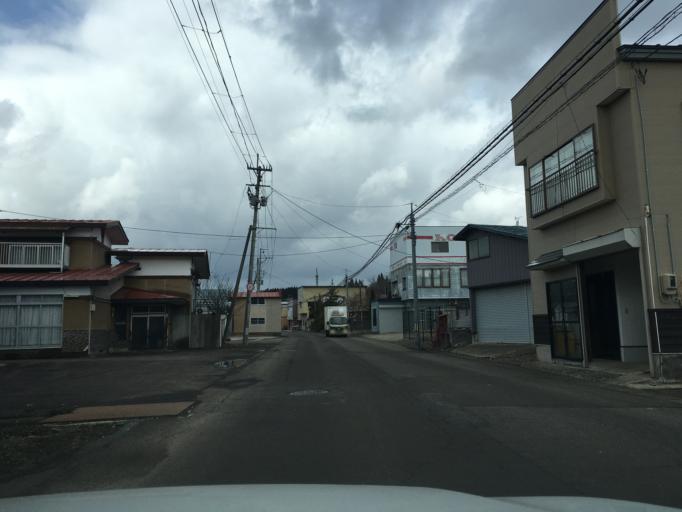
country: JP
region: Akita
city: Takanosu
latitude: 40.1585
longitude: 140.3328
